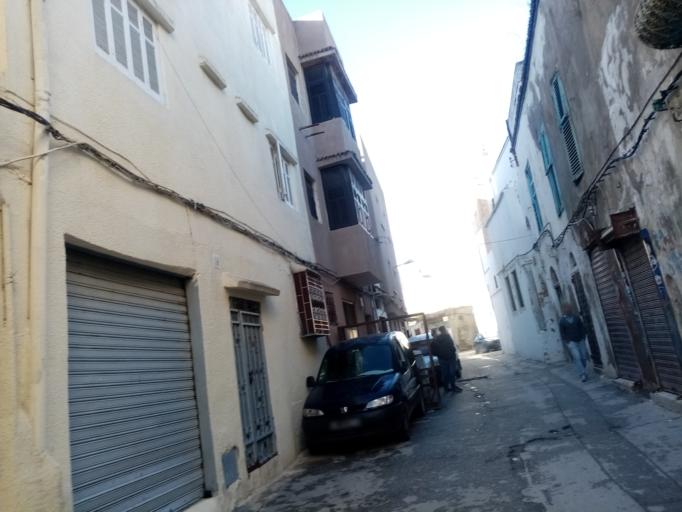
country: TN
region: Tunis
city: Tunis
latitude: 36.7901
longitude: 10.1761
